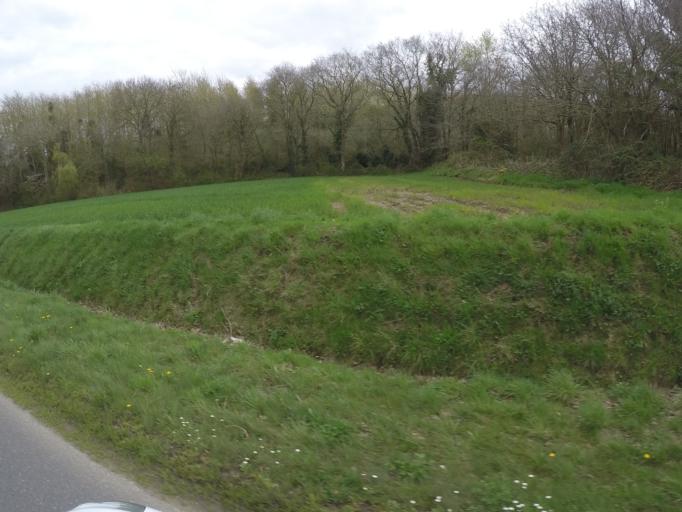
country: FR
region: Brittany
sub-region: Departement des Cotes-d'Armor
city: Plouha
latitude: 48.6620
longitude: -2.9515
